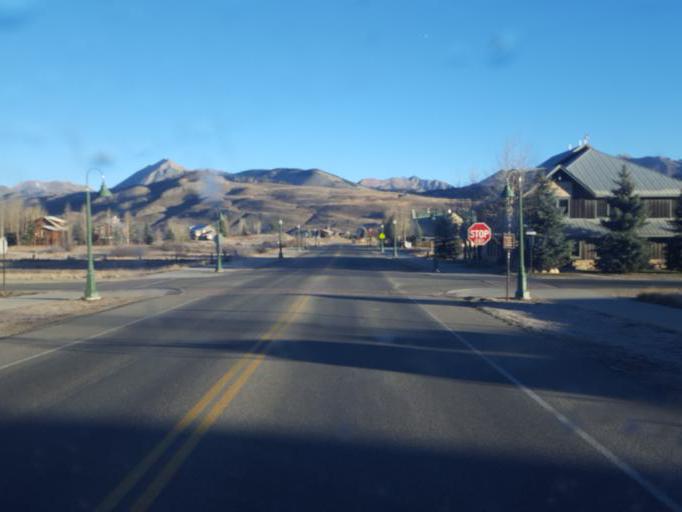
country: US
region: Colorado
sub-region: Gunnison County
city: Crested Butte
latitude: 38.8712
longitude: -106.9809
